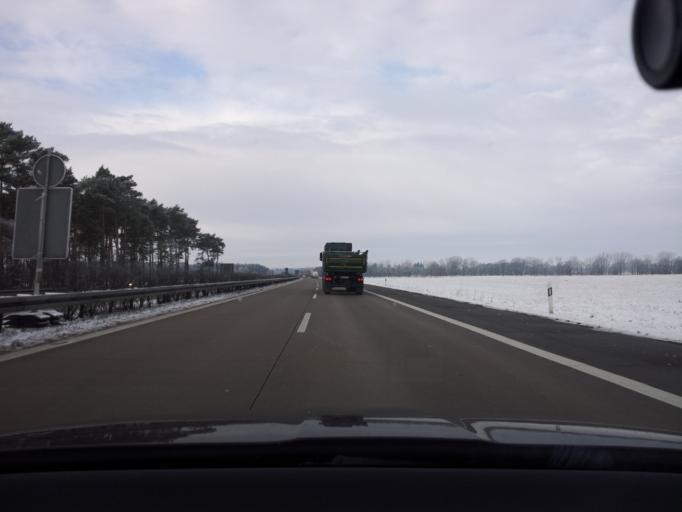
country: DE
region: Mecklenburg-Vorpommern
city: Rastow
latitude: 53.4313
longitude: 11.4875
